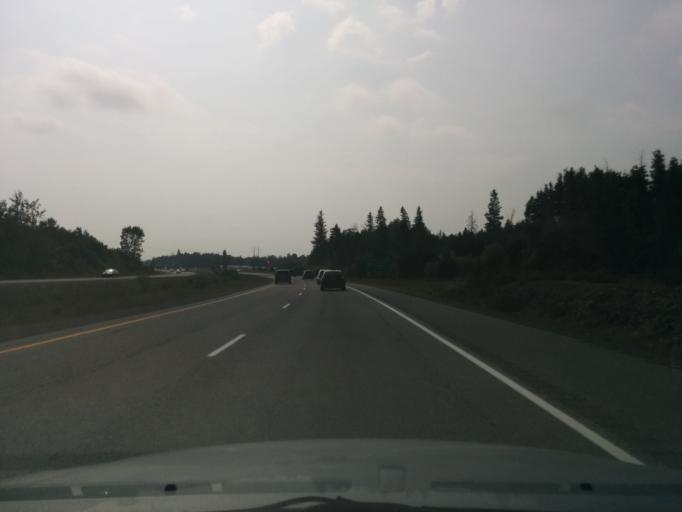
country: CA
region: Ontario
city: Bells Corners
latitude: 45.2836
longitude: -75.8058
